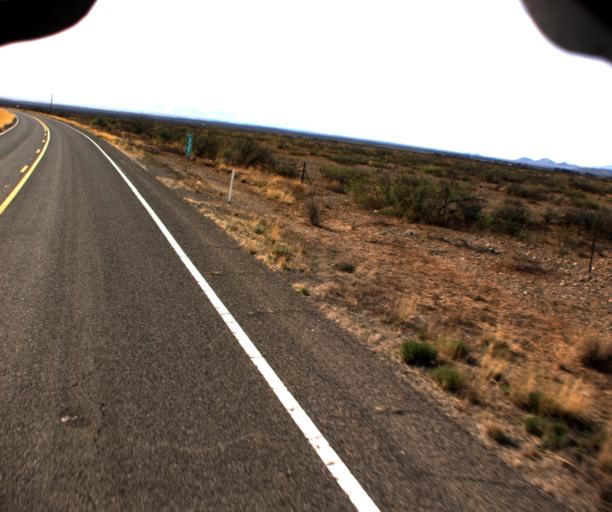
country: US
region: Arizona
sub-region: Cochise County
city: Willcox
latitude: 32.1949
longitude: -109.7085
